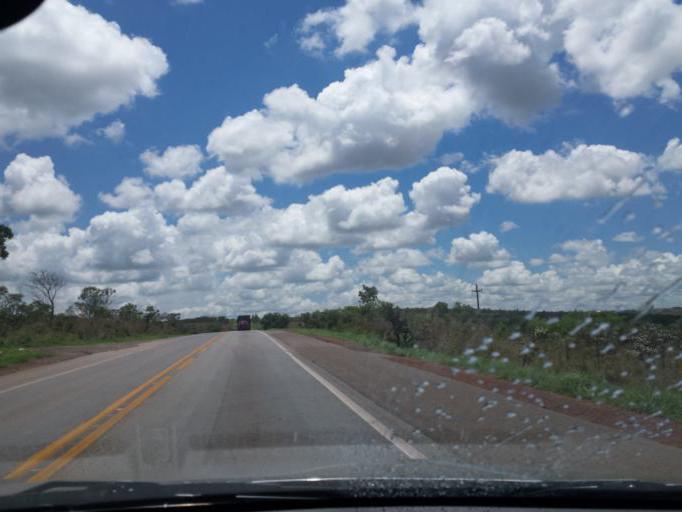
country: BR
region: Goias
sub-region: Cristalina
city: Cristalina
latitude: -16.7245
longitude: -47.6420
